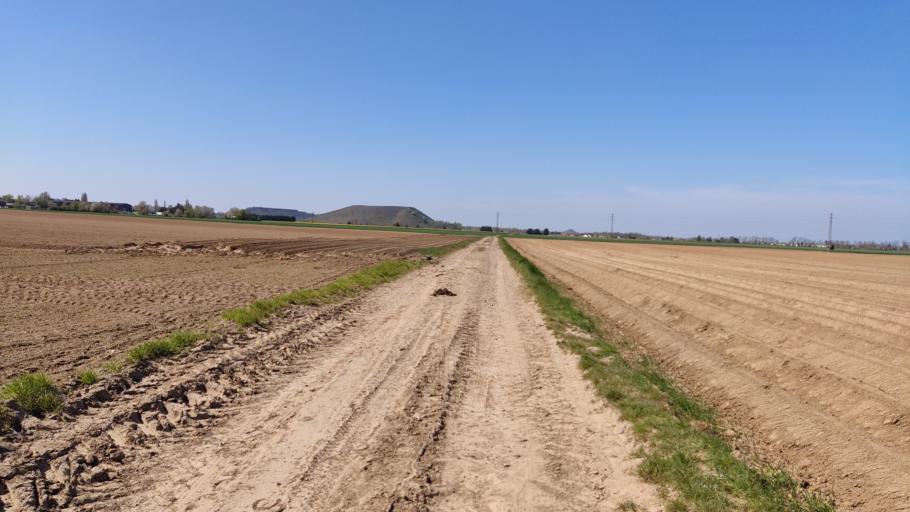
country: FR
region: Nord-Pas-de-Calais
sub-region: Departement du Pas-de-Calais
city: Henin-Beaumont
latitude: 50.3956
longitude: 2.9553
